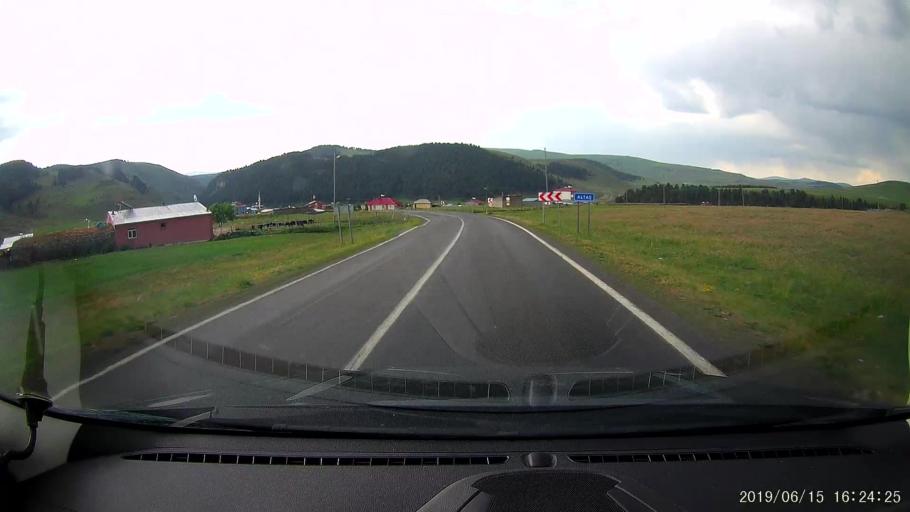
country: TR
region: Ardahan
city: Hanak
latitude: 41.1651
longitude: 42.8702
